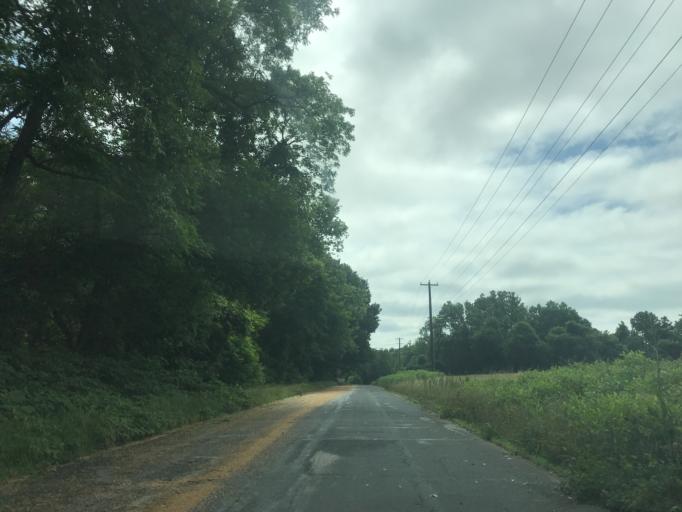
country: US
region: Maryland
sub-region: Caroline County
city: Ridgely
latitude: 38.9226
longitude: -75.9741
